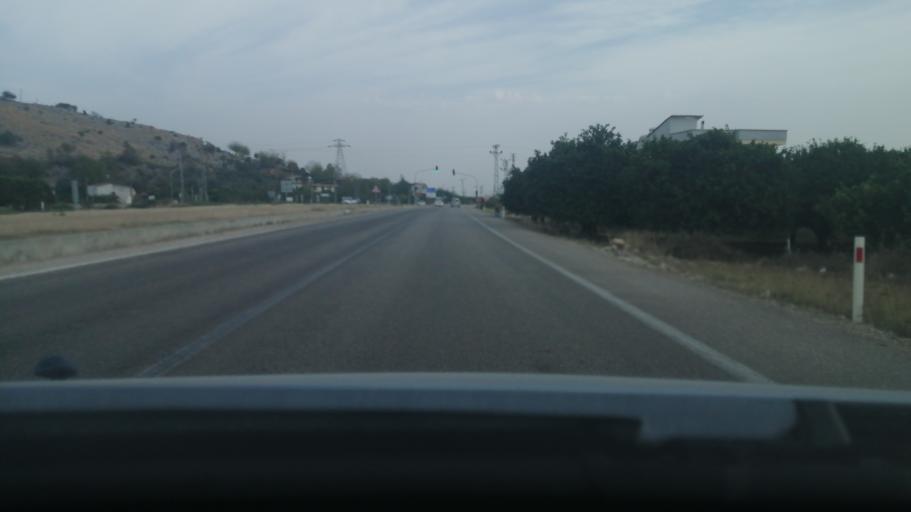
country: TR
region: Adana
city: Kozan
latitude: 37.3805
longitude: 35.8247
